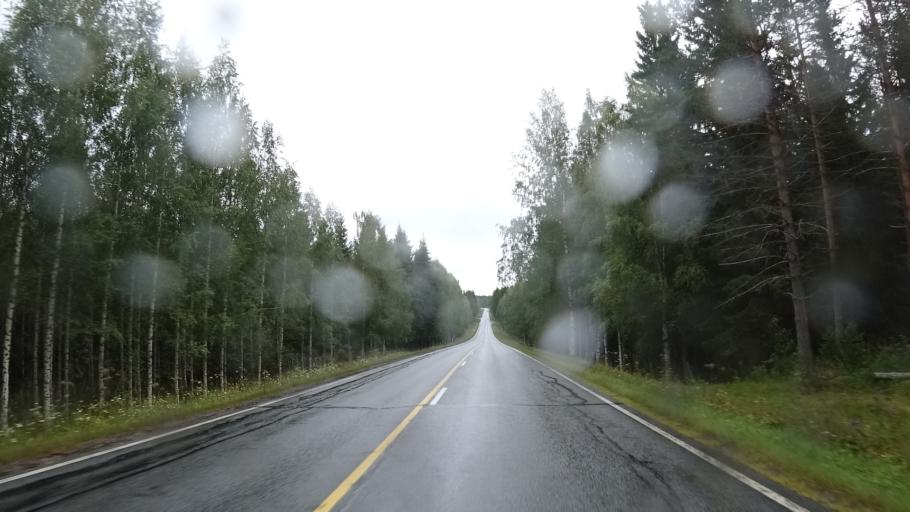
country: FI
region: North Karelia
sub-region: Keski-Karjala
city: Raeaekkylae
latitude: 62.0510
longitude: 29.5953
